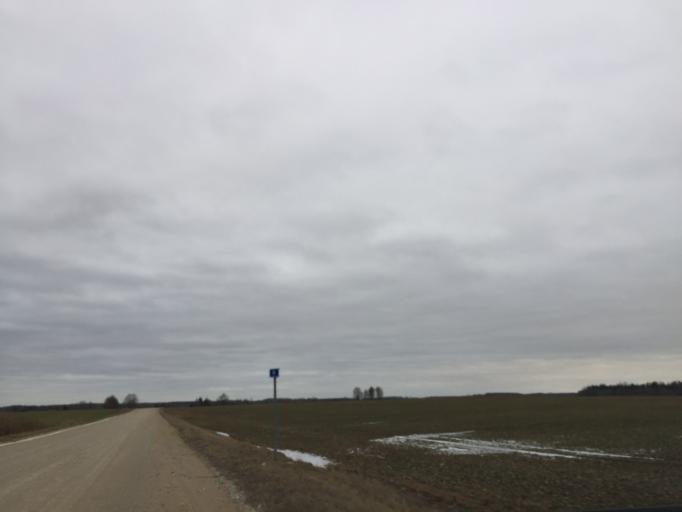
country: LT
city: Zagare
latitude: 56.2822
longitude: 23.2591
